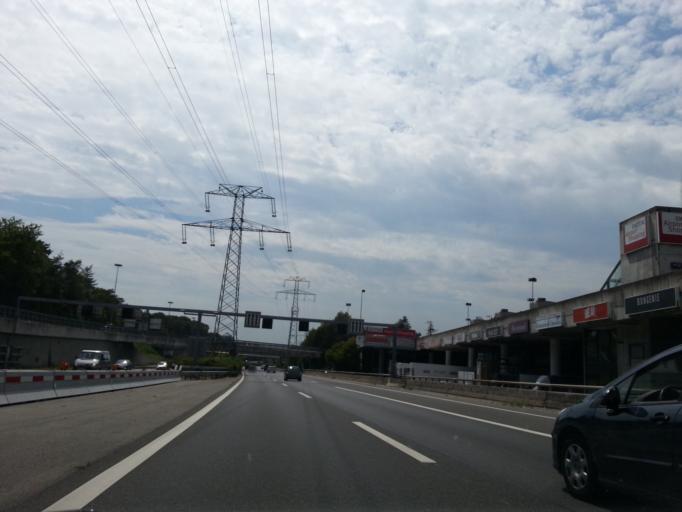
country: CH
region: Geneva
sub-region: Geneva
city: Le Grand-Saconnex
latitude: 46.2333
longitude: 6.1137
